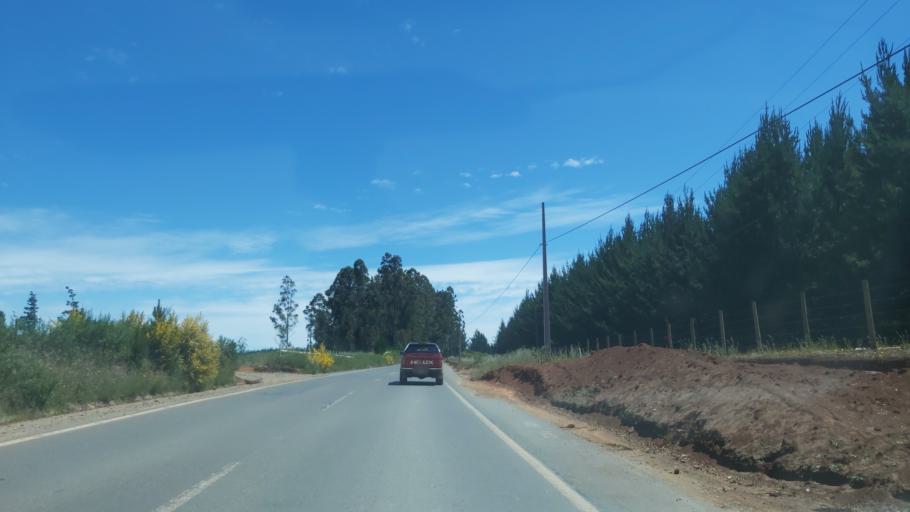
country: CL
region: Maule
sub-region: Provincia de Talca
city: Constitucion
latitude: -35.3951
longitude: -72.4293
